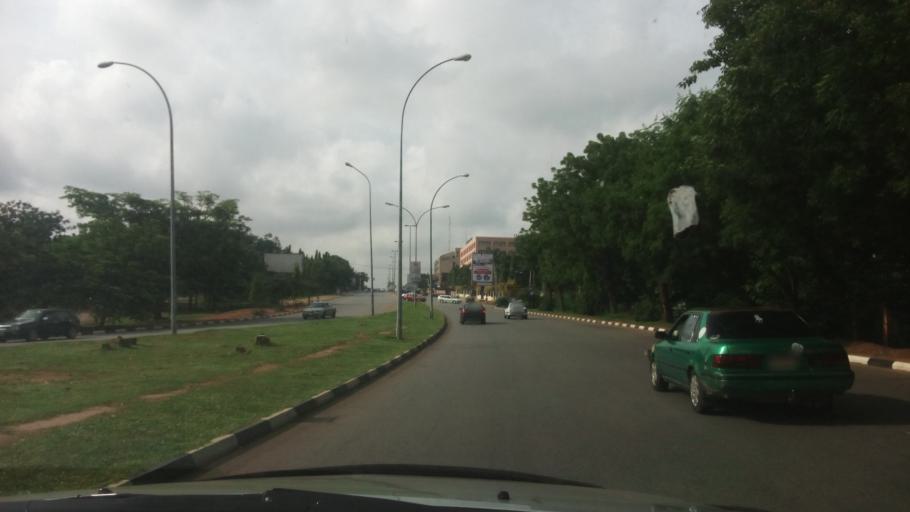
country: NG
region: Abuja Federal Capital Territory
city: Abuja
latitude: 9.0691
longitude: 7.4956
